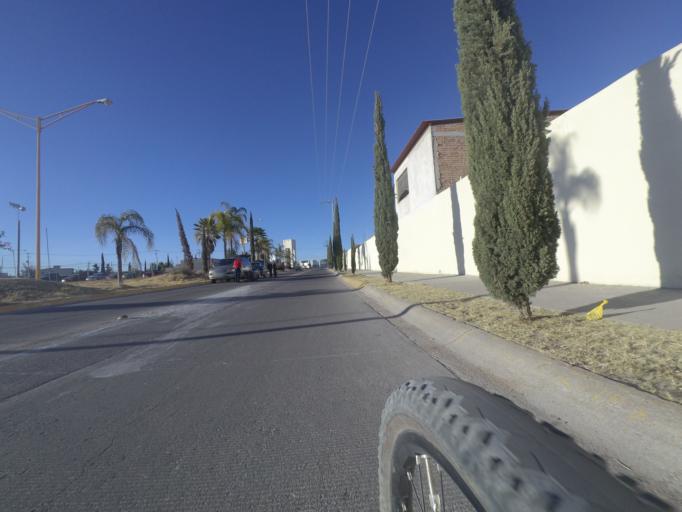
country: MX
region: Aguascalientes
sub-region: Aguascalientes
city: La Loma de los Negritos
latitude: 21.8565
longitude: -102.3454
